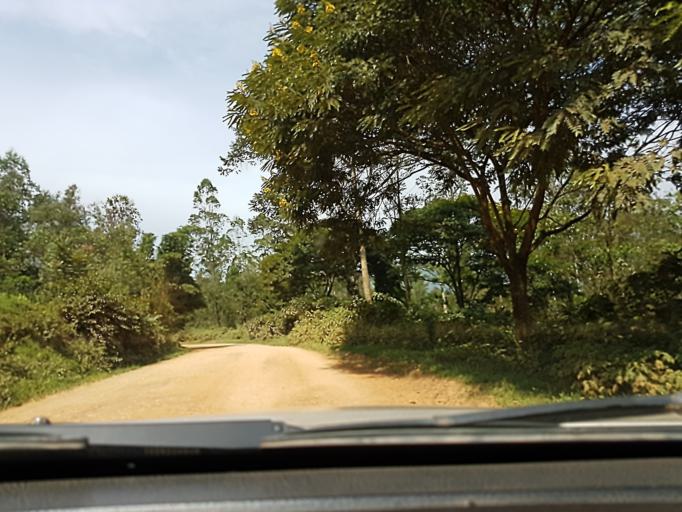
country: CD
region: South Kivu
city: Bukavu
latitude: -2.6448
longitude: 28.8761
